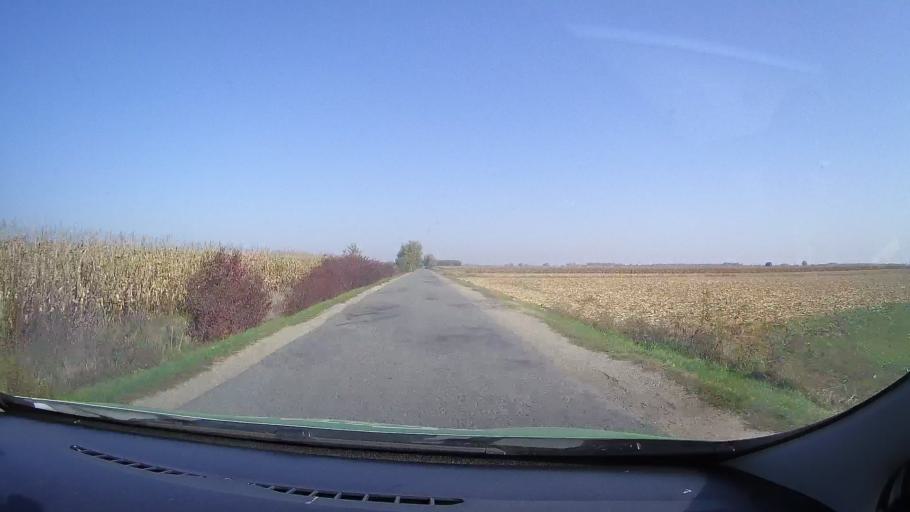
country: RO
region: Satu Mare
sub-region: Comuna Ciumesti
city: Ciumesti
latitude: 47.6796
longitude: 22.3473
